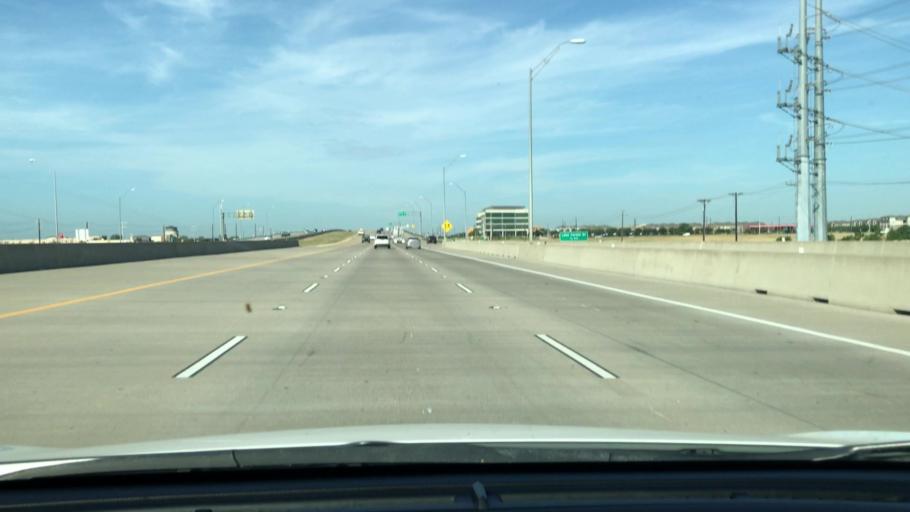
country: US
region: Texas
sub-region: Collin County
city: Fairview
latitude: 33.1472
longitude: -96.6731
